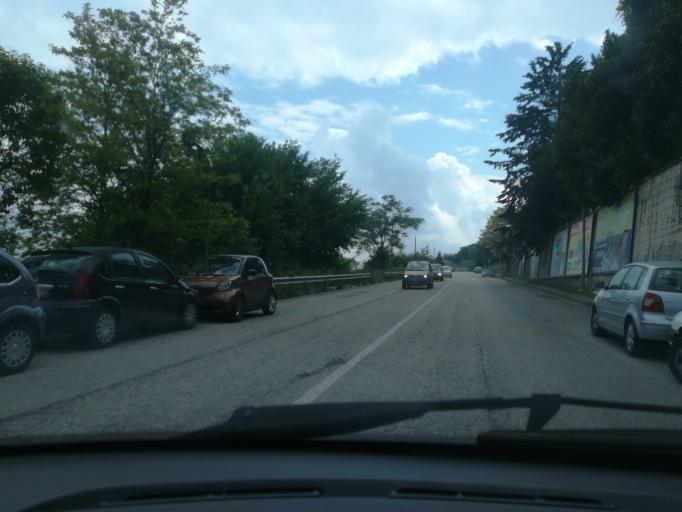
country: IT
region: The Marches
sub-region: Provincia di Macerata
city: Macerata
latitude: 43.3027
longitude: 13.4446
